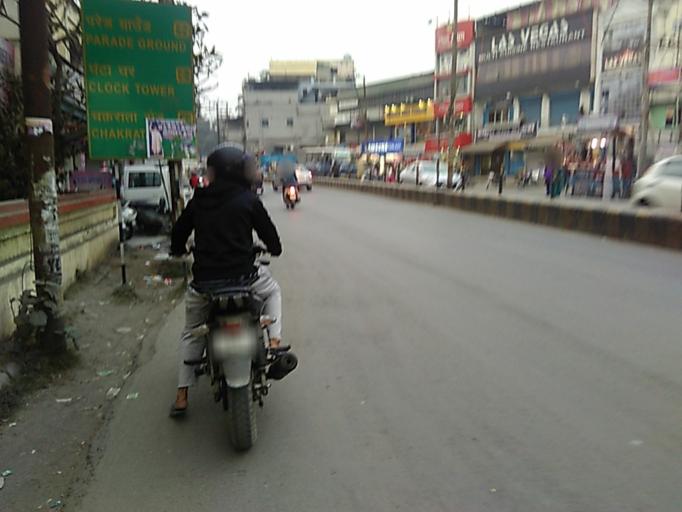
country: IN
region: Uttarakhand
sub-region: Dehradun
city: Dehradun
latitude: 30.3219
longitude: 78.0420
